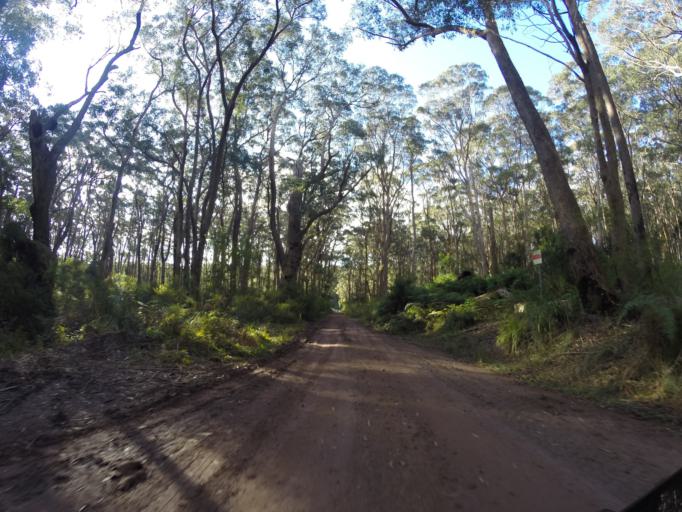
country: AU
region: New South Wales
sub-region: Wollongong
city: Cordeaux Heights
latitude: -34.4078
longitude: 150.7857
